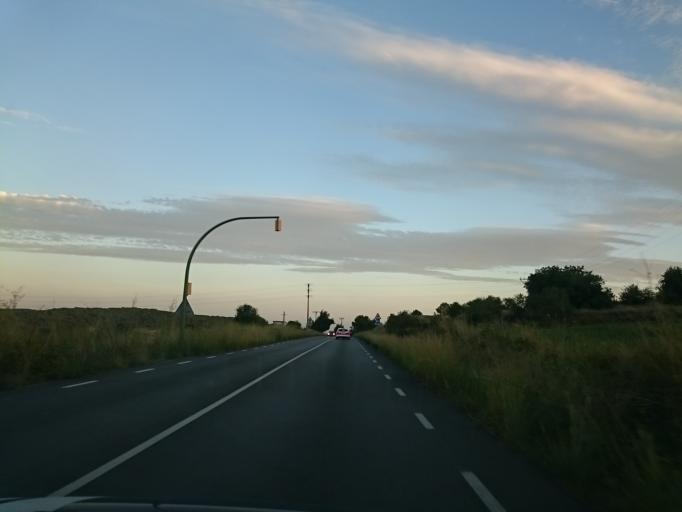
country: ES
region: Catalonia
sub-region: Provincia de Barcelona
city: Sant Pere de Ribes
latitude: 41.2498
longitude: 1.7711
